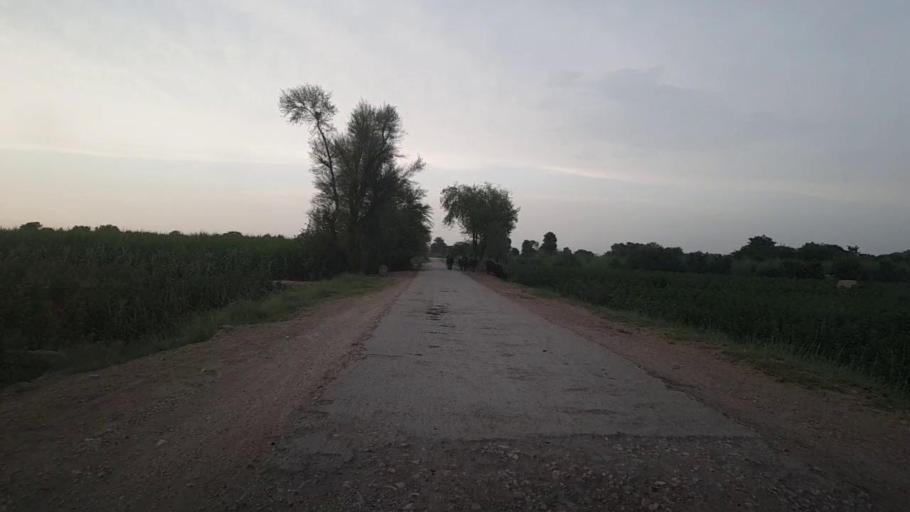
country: PK
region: Sindh
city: Karaundi
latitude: 27.0140
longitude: 68.3539
